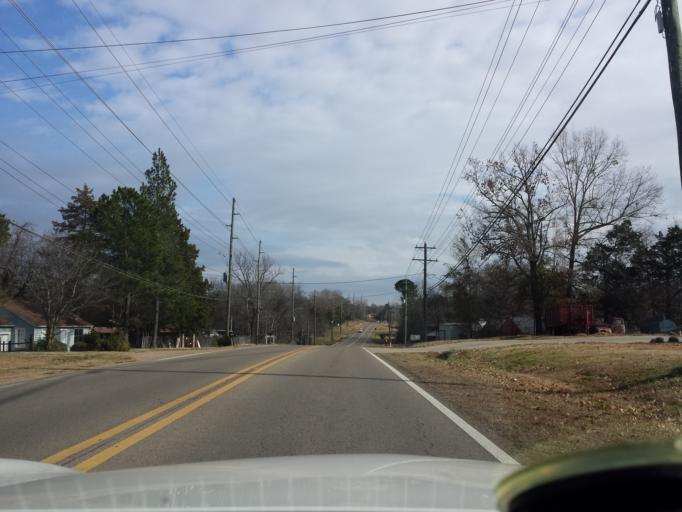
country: US
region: Mississippi
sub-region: Oktibbeha County
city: Starkville
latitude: 33.4649
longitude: -88.8281
